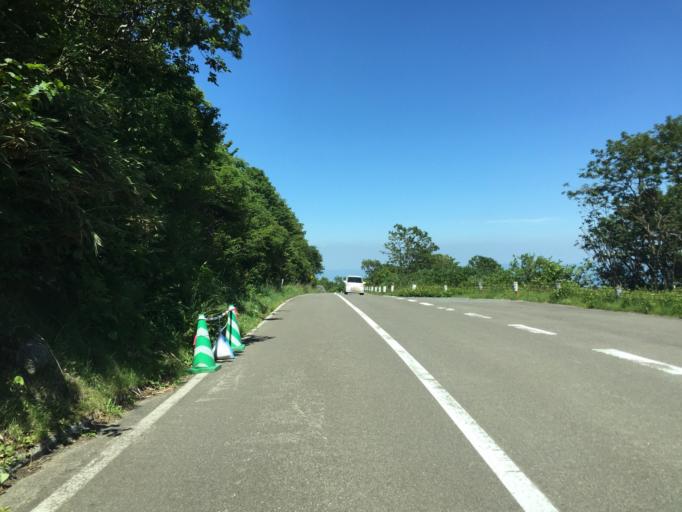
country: JP
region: Fukushima
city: Fukushima-shi
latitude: 37.7406
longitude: 140.2703
